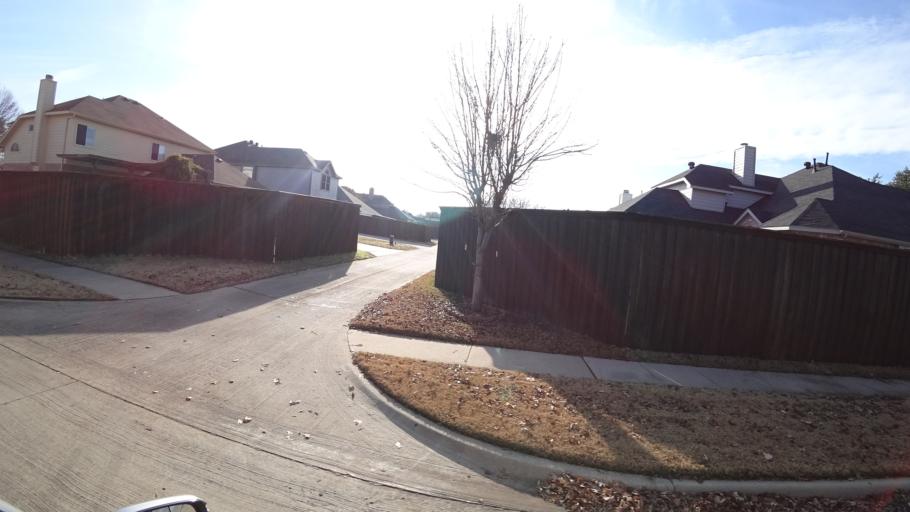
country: US
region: Texas
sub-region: Denton County
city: Lewisville
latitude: 33.0606
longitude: -97.0211
